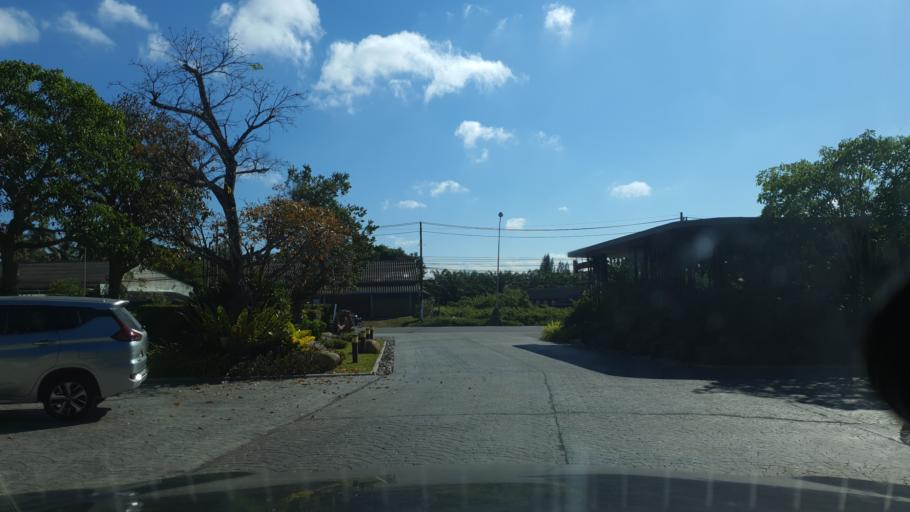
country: TH
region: Phangnga
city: Ban Ao Nang
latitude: 8.0346
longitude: 98.8610
